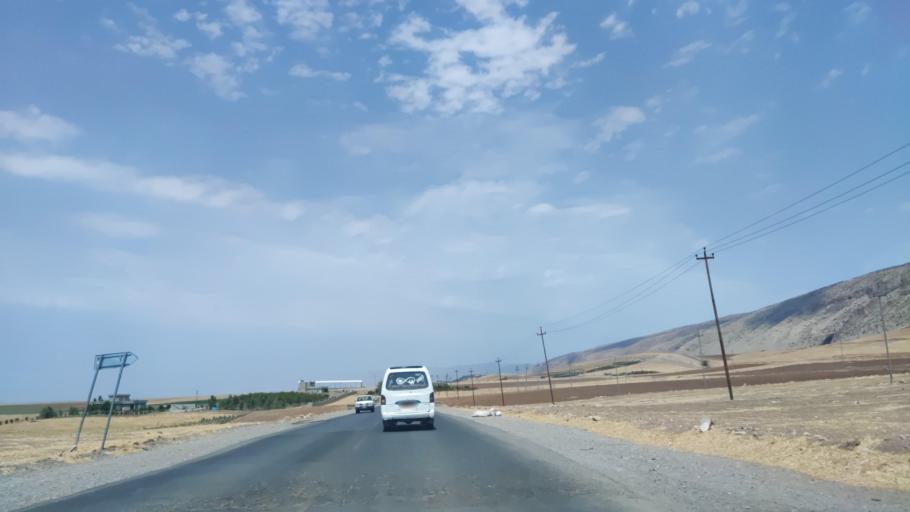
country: IQ
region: Arbil
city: Shaqlawah
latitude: 36.5116
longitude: 44.3763
